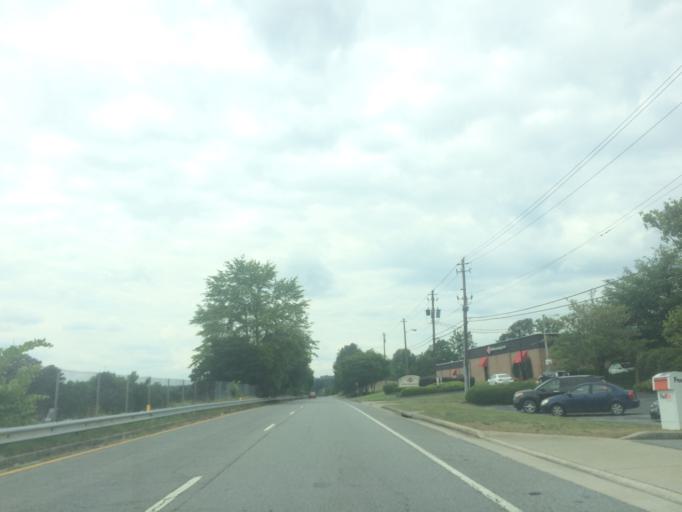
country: US
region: Georgia
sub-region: DeKalb County
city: Chamblee
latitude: 33.8550
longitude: -84.2973
